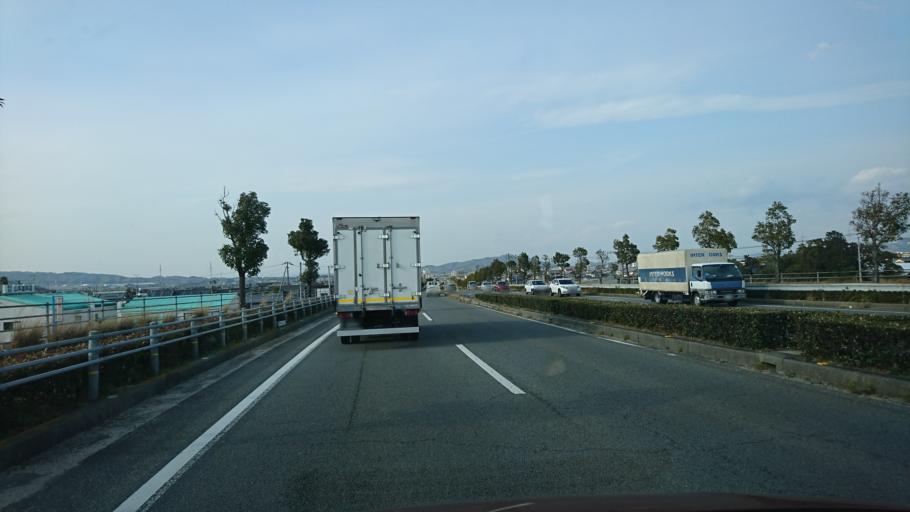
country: JP
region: Ehime
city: Saijo
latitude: 34.0225
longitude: 133.0109
